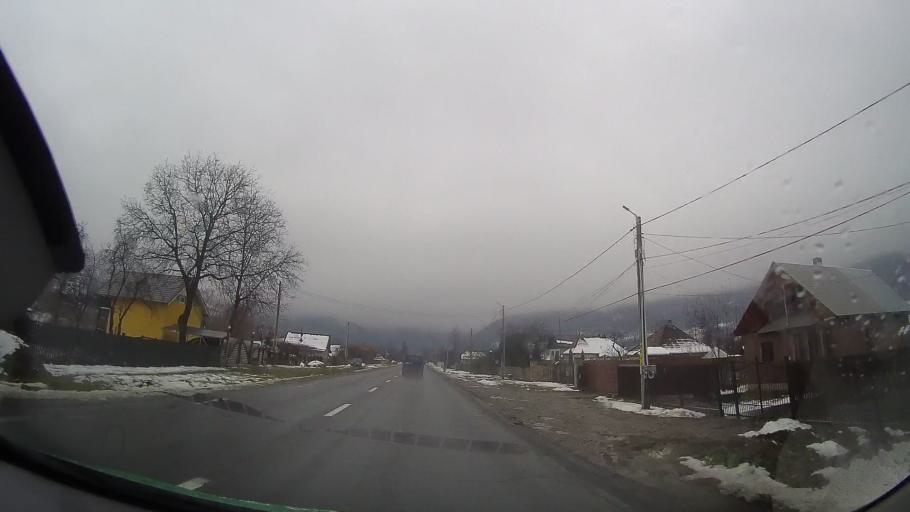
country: RO
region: Neamt
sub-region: Comuna Pangarati
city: Stejaru
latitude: 46.9071
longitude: 26.1770
